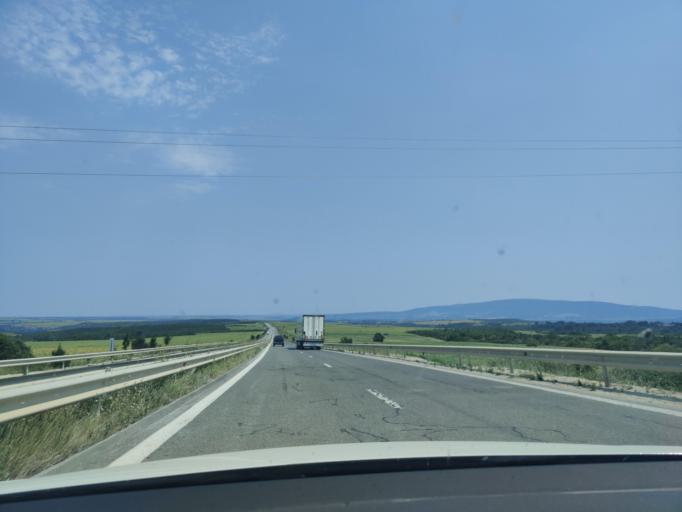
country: BG
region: Montana
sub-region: Obshtina Montana
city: Montana
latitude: 43.4240
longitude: 23.1653
